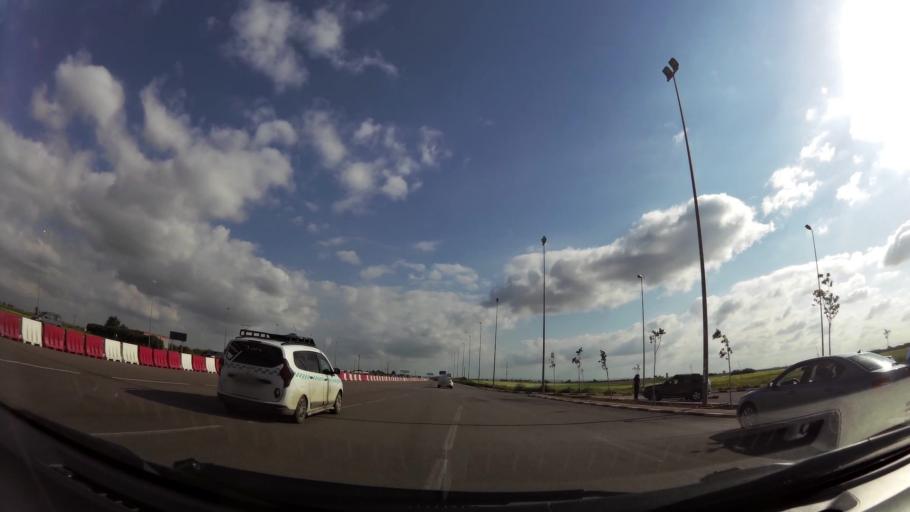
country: MA
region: Chaouia-Ouardigha
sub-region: Settat Province
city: Berrechid
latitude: 33.2309
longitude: -7.5731
